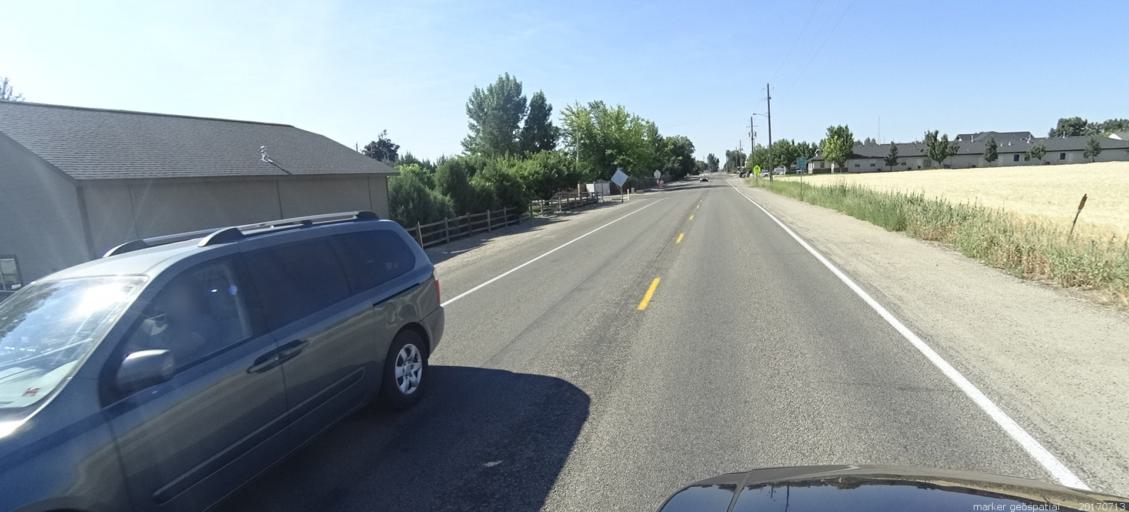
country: US
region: Idaho
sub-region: Ada County
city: Kuna
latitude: 43.4987
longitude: -116.4137
